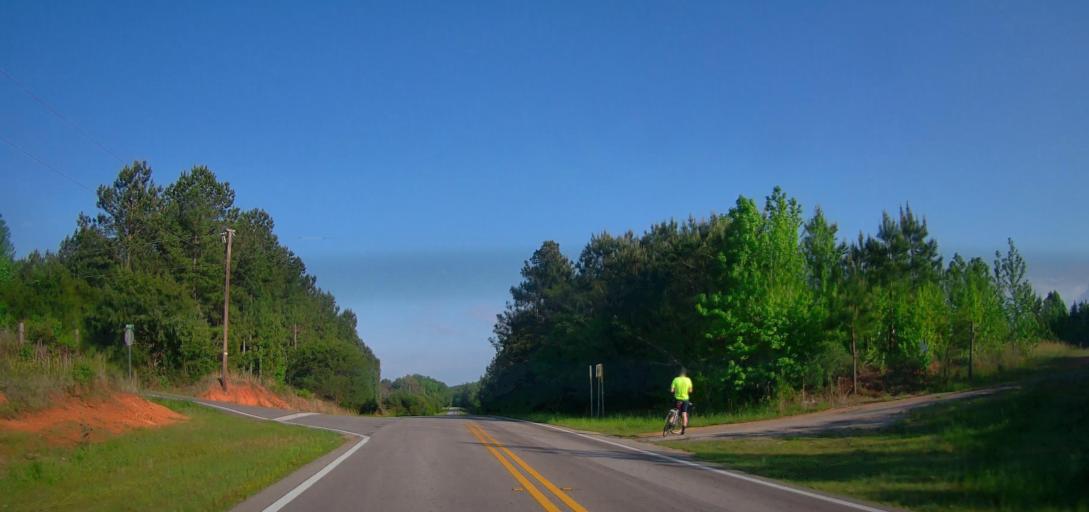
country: US
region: Georgia
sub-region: Putnam County
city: Eatonton
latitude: 33.3056
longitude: -83.3449
